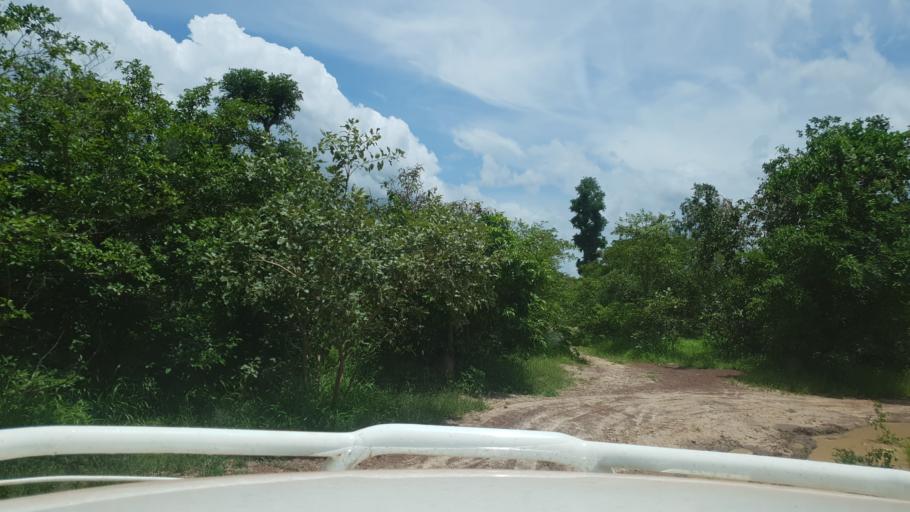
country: ML
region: Koulikoro
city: Banamba
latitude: 13.2008
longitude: -7.3356
